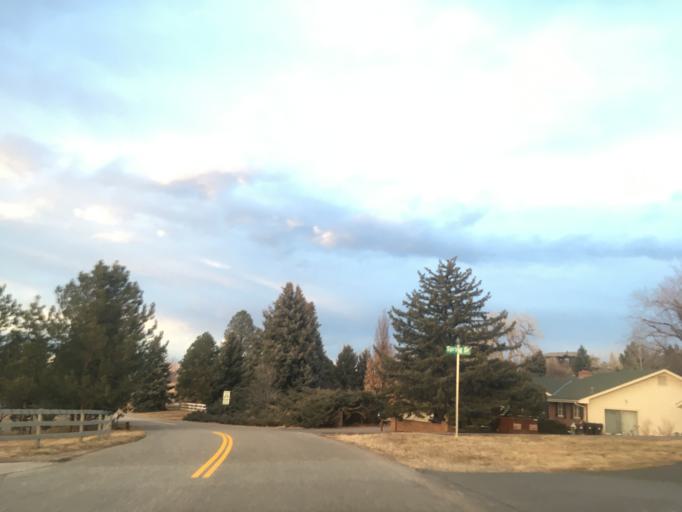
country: US
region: Colorado
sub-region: Boulder County
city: Superior
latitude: 39.9829
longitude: -105.1744
